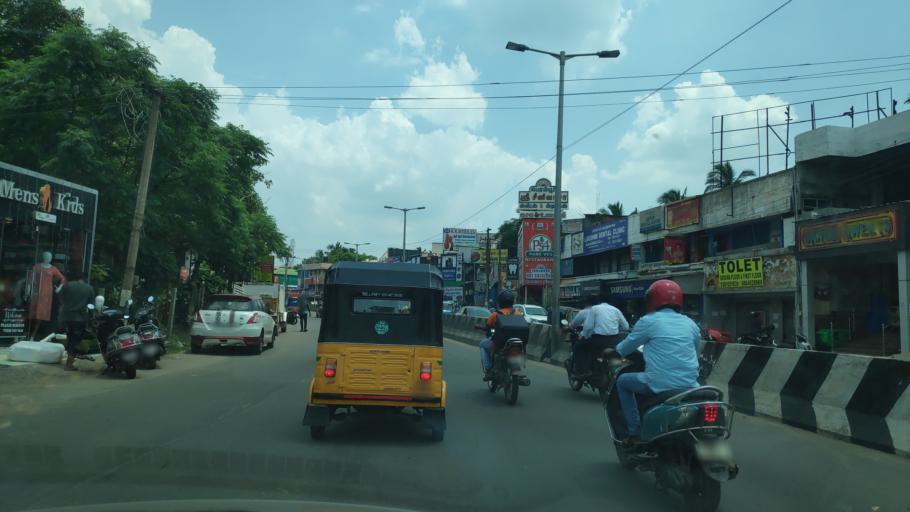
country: IN
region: Tamil Nadu
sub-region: Thiruvallur
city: Ambattur
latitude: 13.1213
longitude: 80.1487
